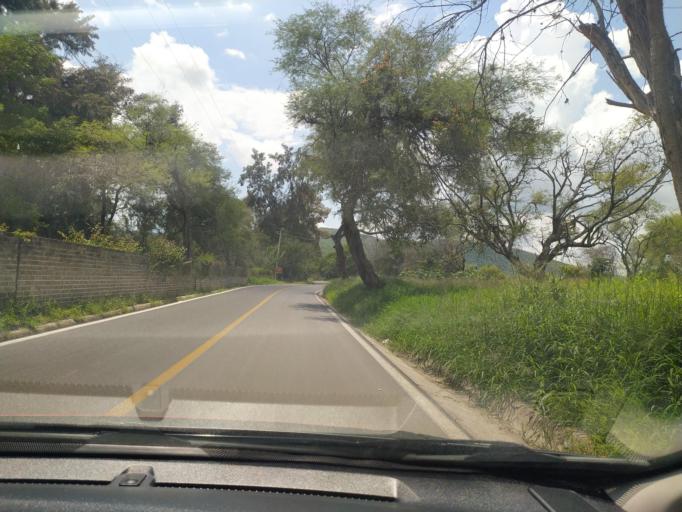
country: MX
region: Jalisco
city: Villa Corona
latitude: 20.4126
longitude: -103.6720
